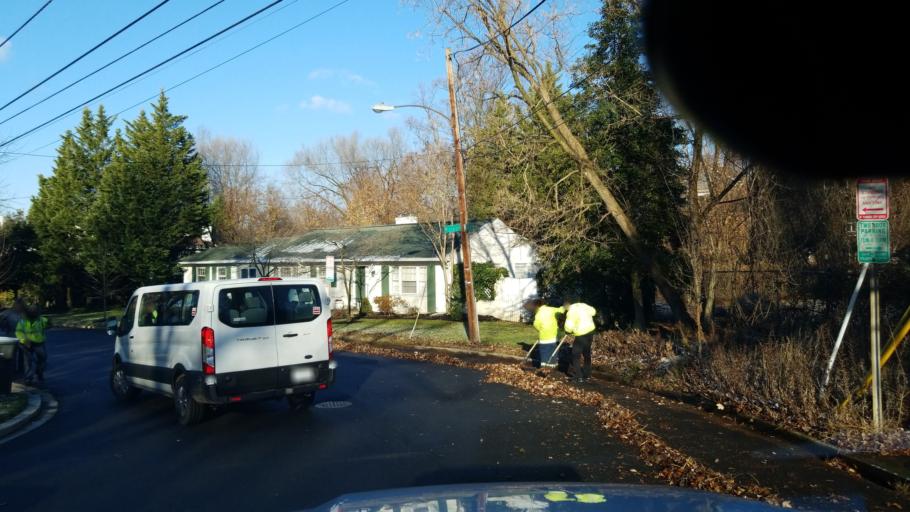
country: US
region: Maryland
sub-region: Montgomery County
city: Friendship Village
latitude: 38.9421
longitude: -77.0866
